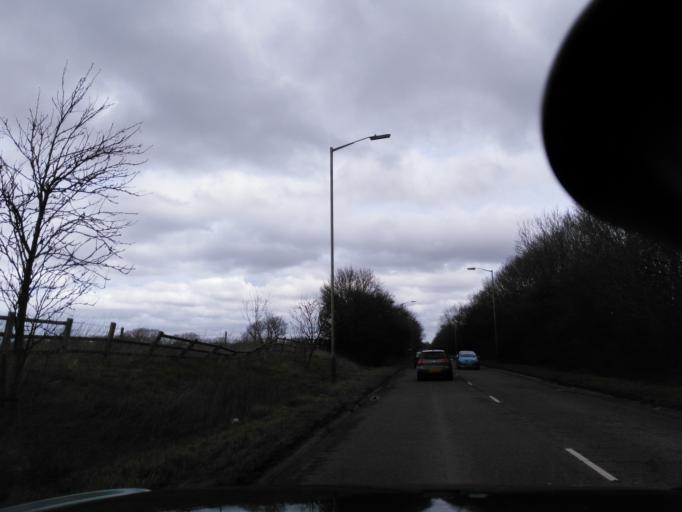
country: GB
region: England
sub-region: Wiltshire
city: Melksham
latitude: 51.3701
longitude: -2.1455
